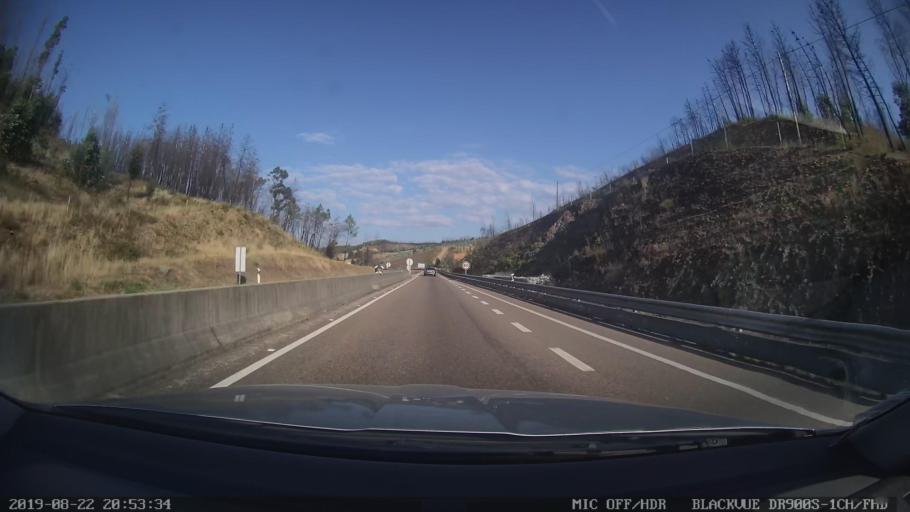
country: PT
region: Castelo Branco
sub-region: Proenca-A-Nova
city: Proenca-a-Nova
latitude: 39.7714
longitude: -7.9949
